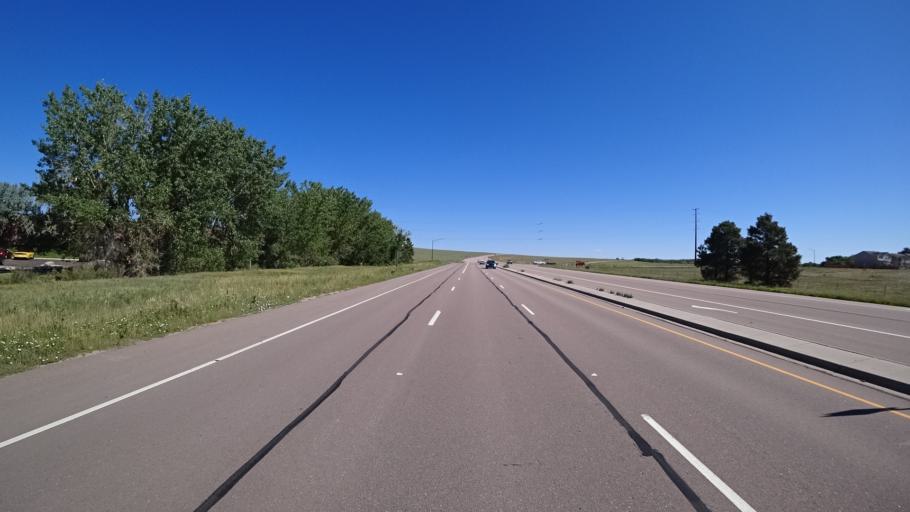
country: US
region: Colorado
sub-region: El Paso County
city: Security-Widefield
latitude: 38.7793
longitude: -104.6598
